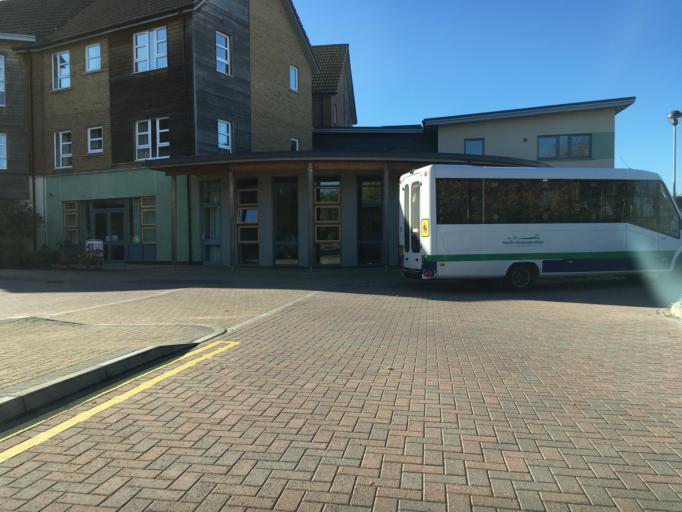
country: GB
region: England
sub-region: South Gloucestershire
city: Yate
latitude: 51.5483
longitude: -2.4173
